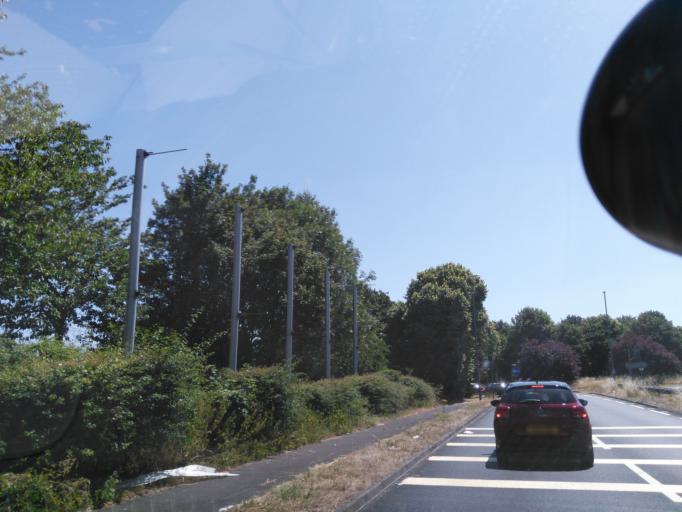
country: GB
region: England
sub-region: Bath and North East Somerset
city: Keynsham
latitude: 51.4131
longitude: -2.4838
